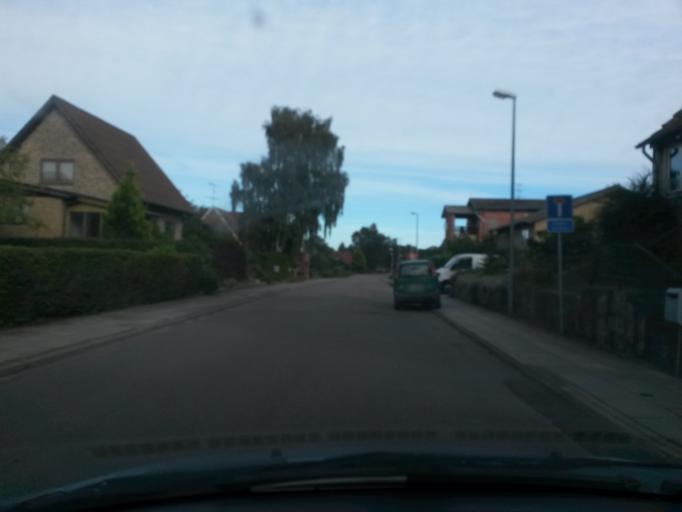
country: DK
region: Central Jutland
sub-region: Silkeborg Kommune
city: Kjellerup
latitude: 56.2897
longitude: 9.4366
